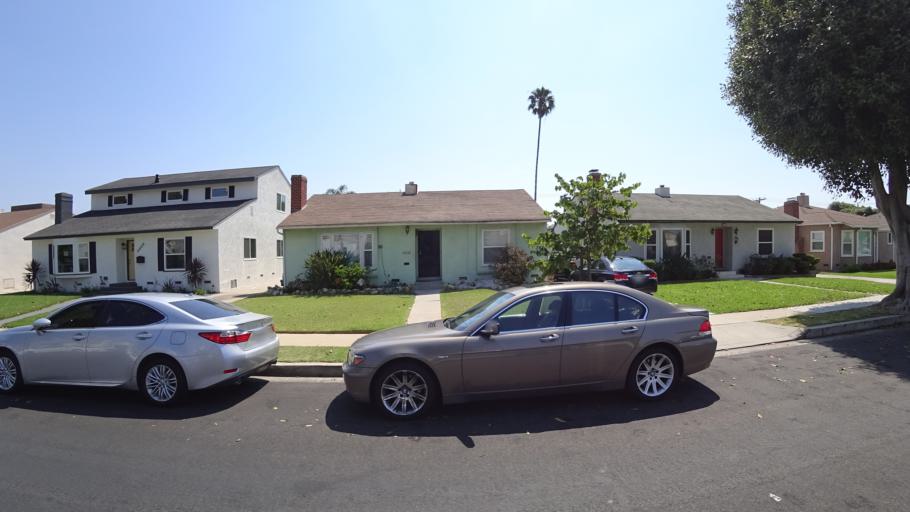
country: US
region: California
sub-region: Los Angeles County
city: Westmont
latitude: 33.9575
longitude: -118.3221
